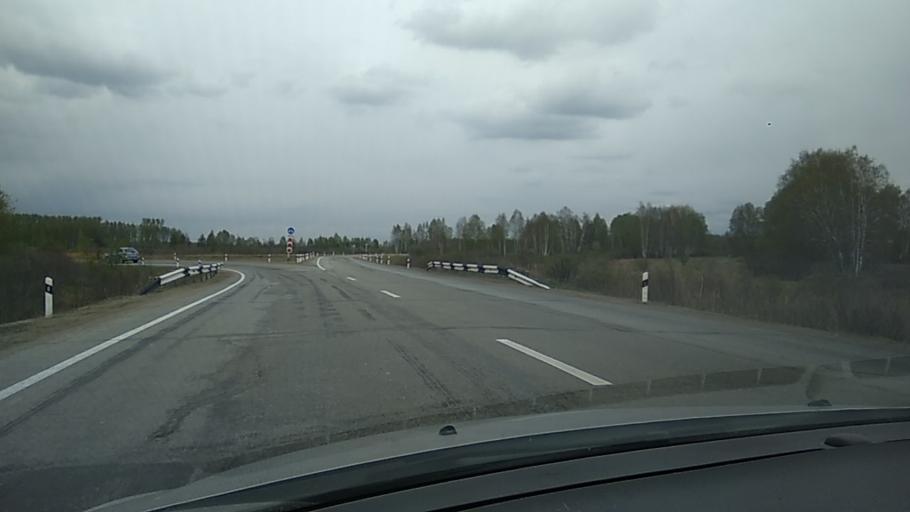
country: RU
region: Sverdlovsk
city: Pokrovskoye
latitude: 56.4619
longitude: 61.7203
